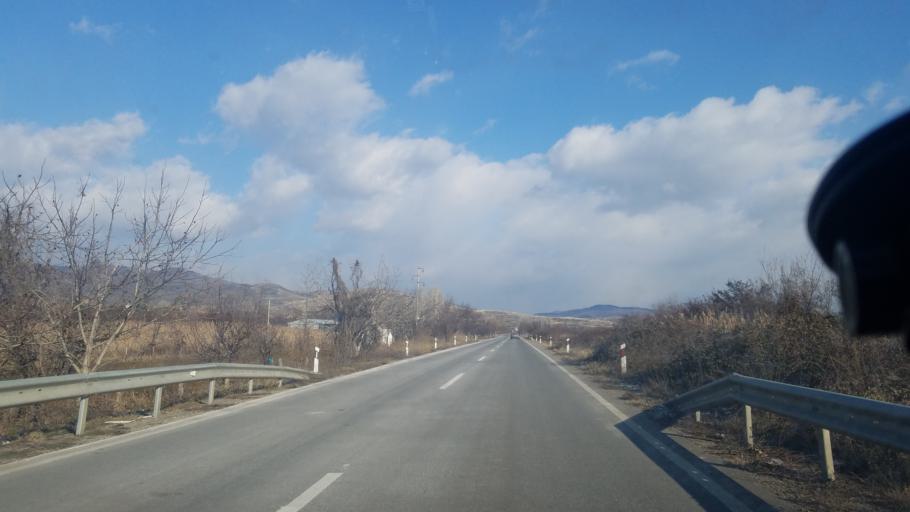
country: MK
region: Kocani
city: Kochani
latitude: 41.9079
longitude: 22.4303
